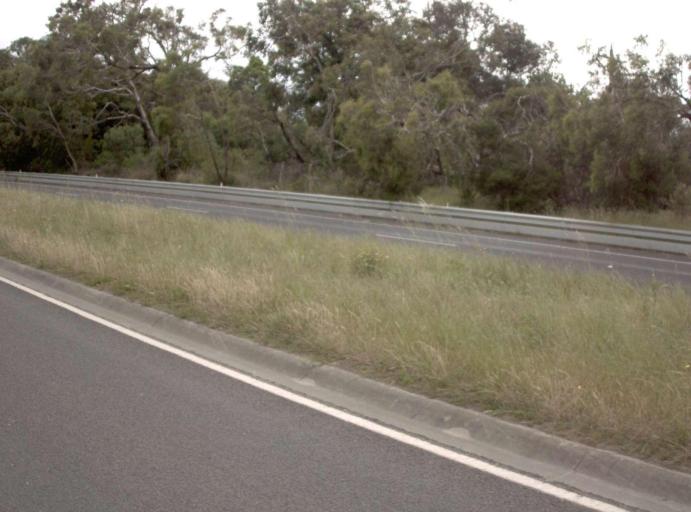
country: AU
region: Victoria
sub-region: Casey
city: Junction Village
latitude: -38.1537
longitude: 145.3169
